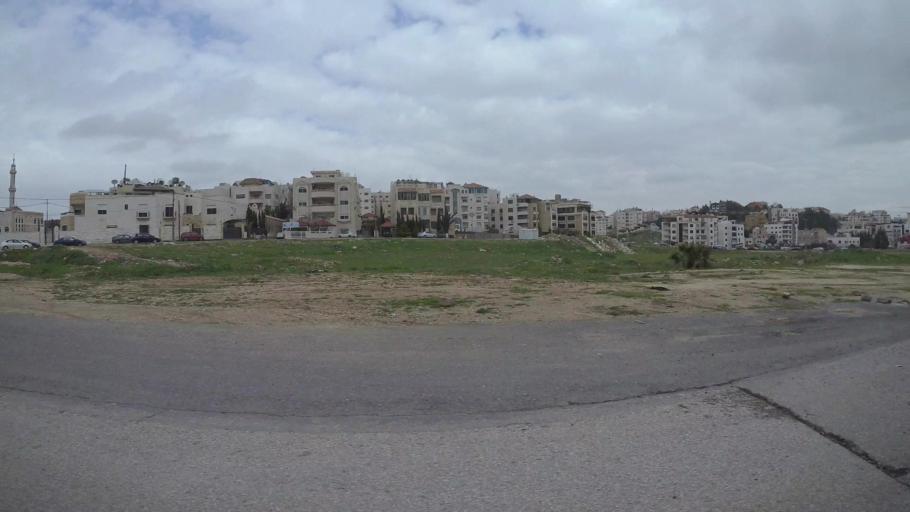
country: JO
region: Amman
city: Wadi as Sir
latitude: 31.9843
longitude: 35.8359
